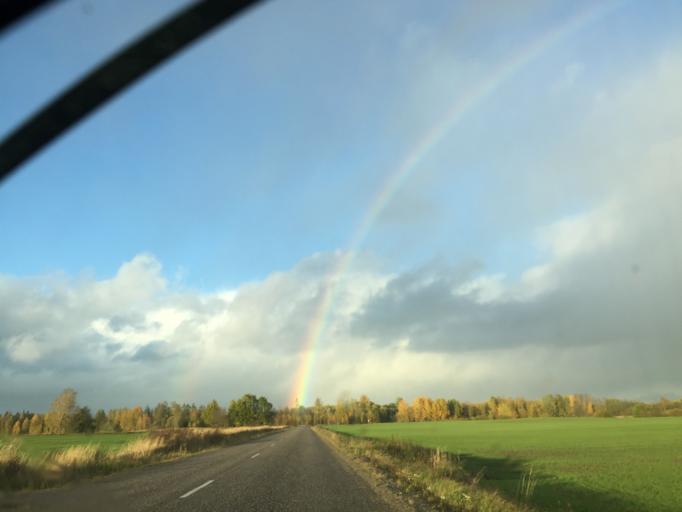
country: LV
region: Broceni
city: Broceni
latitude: 56.8803
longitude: 22.3825
